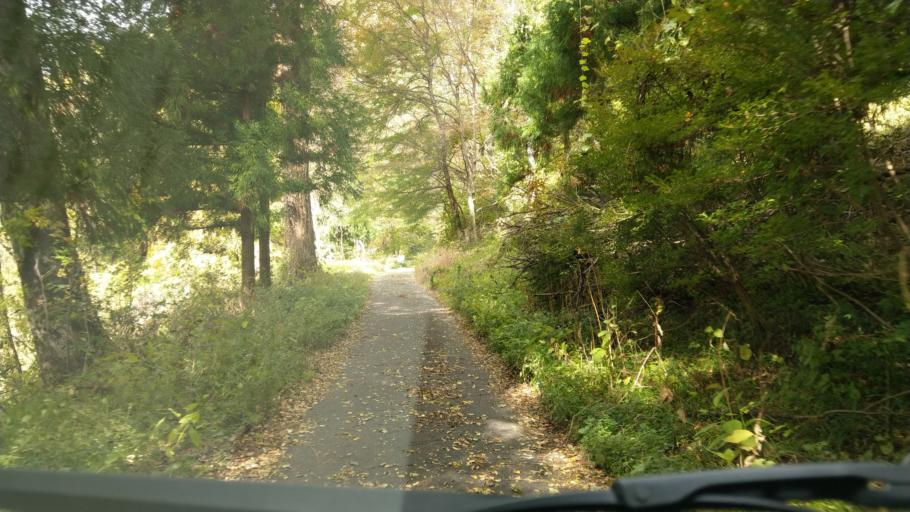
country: JP
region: Nagano
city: Komoro
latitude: 36.3263
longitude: 138.4157
